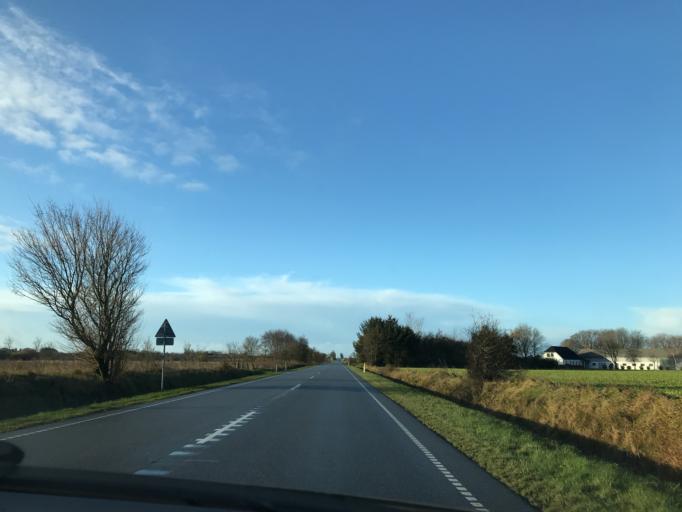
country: DK
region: South Denmark
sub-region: Haderslev Kommune
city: Vojens
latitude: 55.1658
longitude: 9.2894
